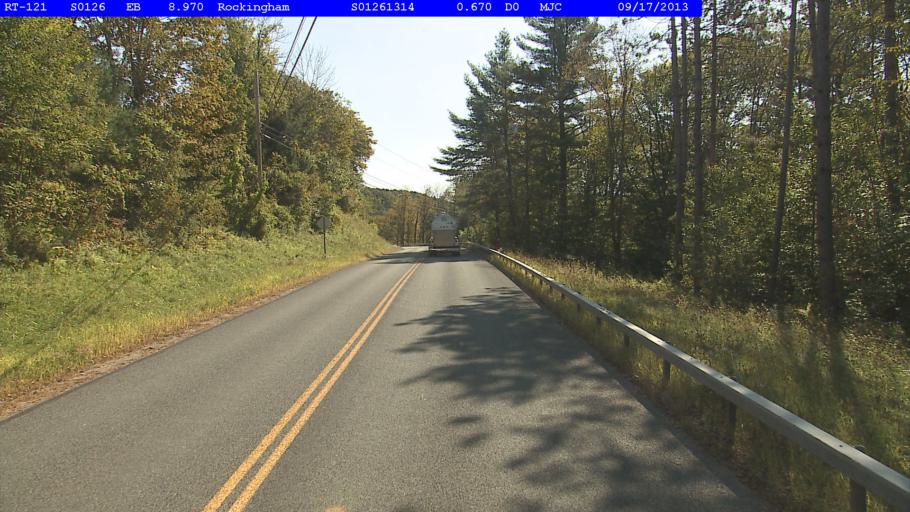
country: US
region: Vermont
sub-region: Windham County
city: Rockingham
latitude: 43.1461
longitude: -72.5470
